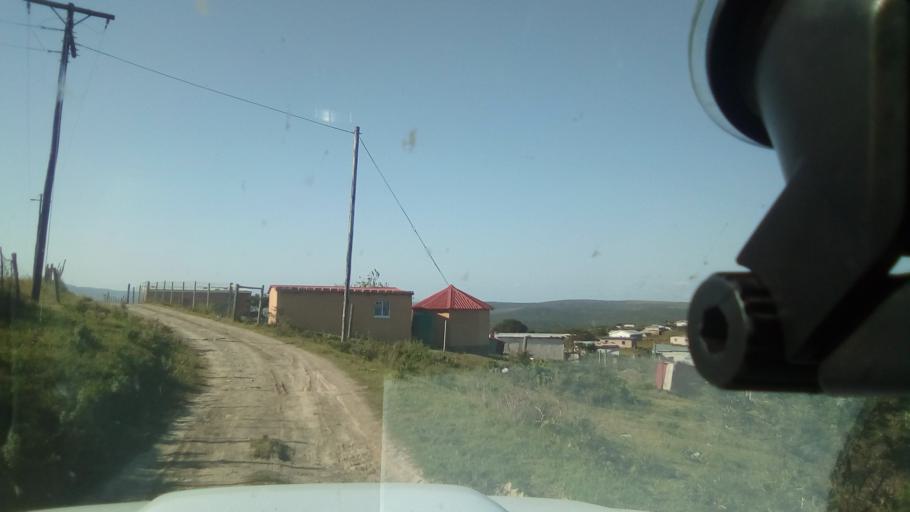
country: ZA
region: Eastern Cape
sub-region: Buffalo City Metropolitan Municipality
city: Bhisho
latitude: -32.7996
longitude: 27.3486
